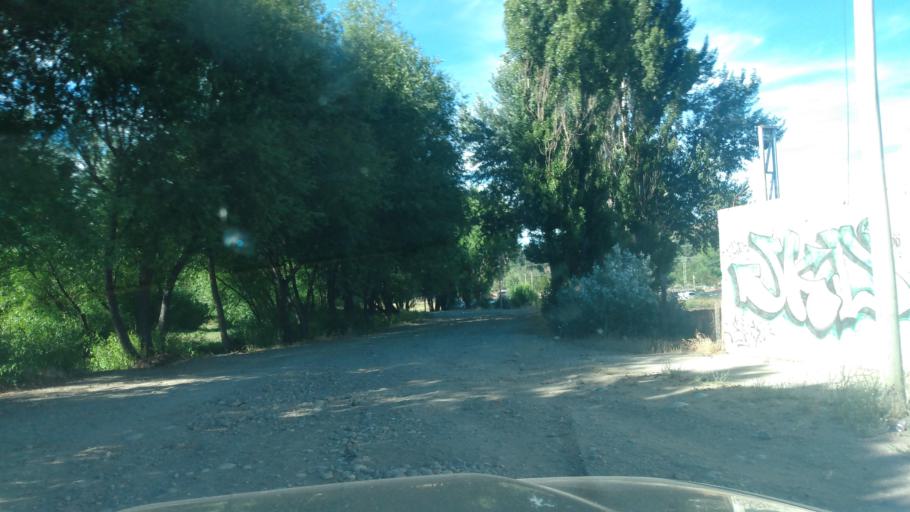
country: AR
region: Neuquen
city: Junin de los Andes
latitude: -39.9594
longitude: -71.0779
